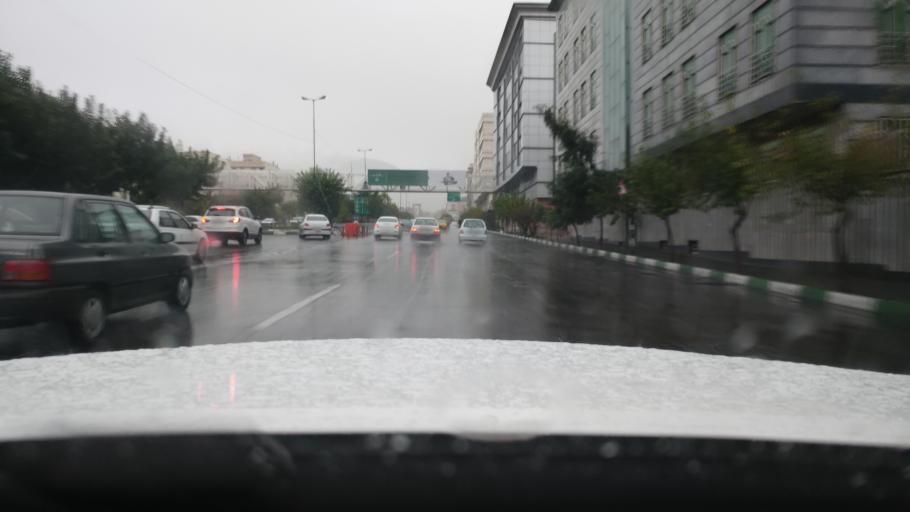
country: IR
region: Tehran
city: Tehran
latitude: 35.7274
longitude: 51.3101
